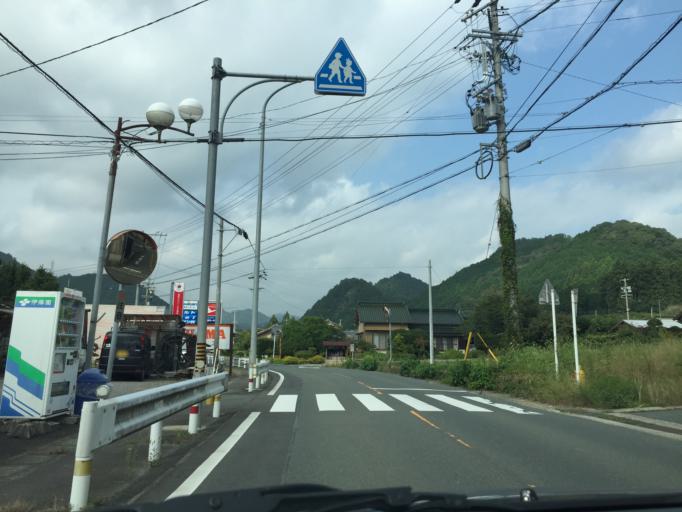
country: JP
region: Aichi
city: Shinshiro
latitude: 34.9587
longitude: 137.6110
